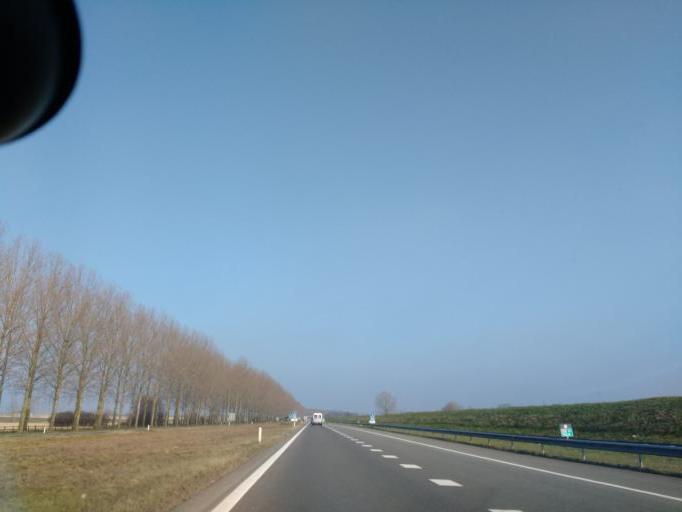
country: NL
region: Gelderland
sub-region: Gemeente Overbetuwe
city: Elst
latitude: 51.8982
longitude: 5.8766
